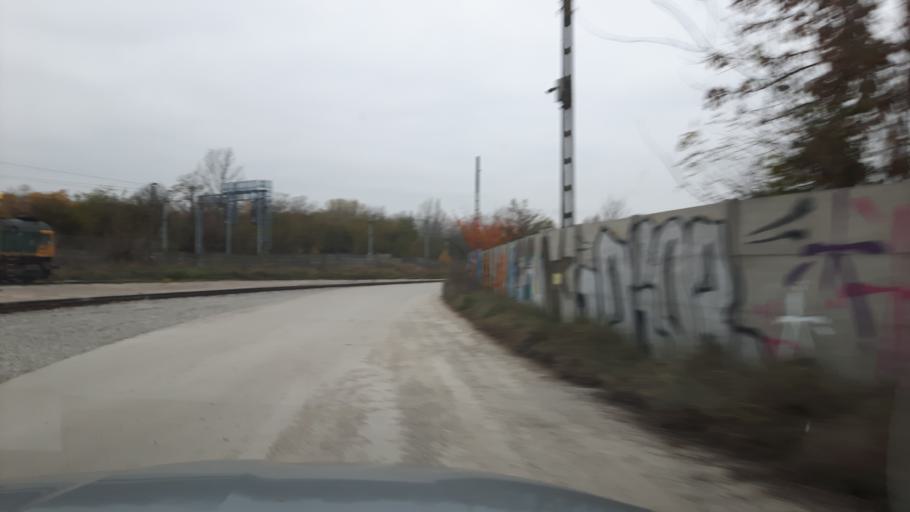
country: PL
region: Masovian Voivodeship
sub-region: Warszawa
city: Praga Polnoc
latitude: 52.2693
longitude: 21.0308
